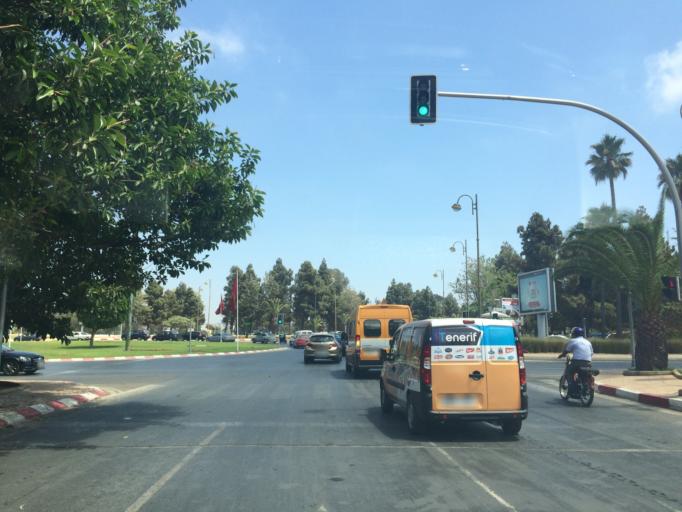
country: MA
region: Rabat-Sale-Zemmour-Zaer
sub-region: Rabat
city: Rabat
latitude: 33.9929
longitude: -6.8396
